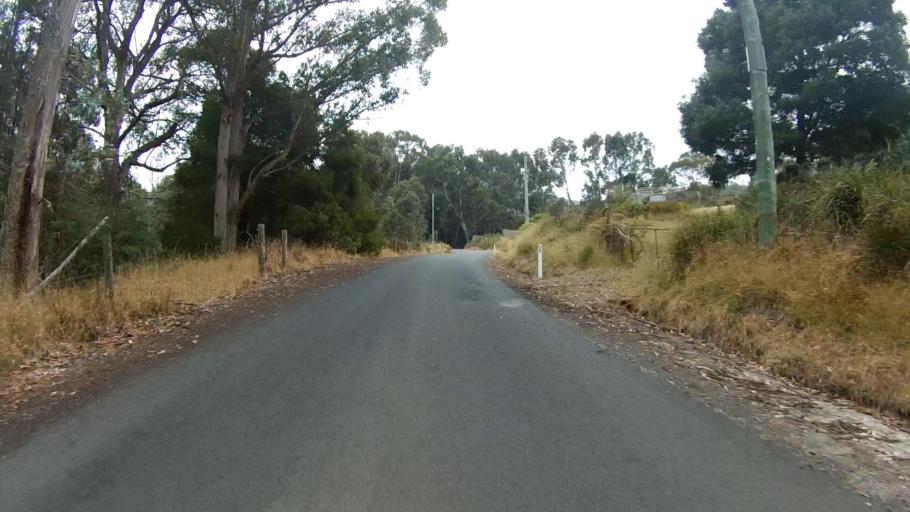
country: AU
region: Tasmania
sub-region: Huon Valley
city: Cygnet
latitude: -43.2360
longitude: 147.1564
